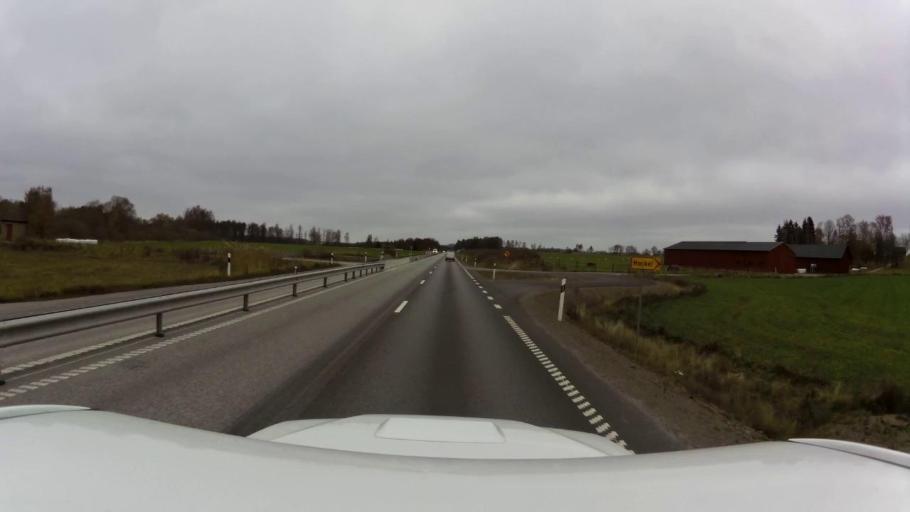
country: SE
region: OEstergoetland
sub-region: Kinda Kommun
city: Rimforsa
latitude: 58.1441
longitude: 15.6810
